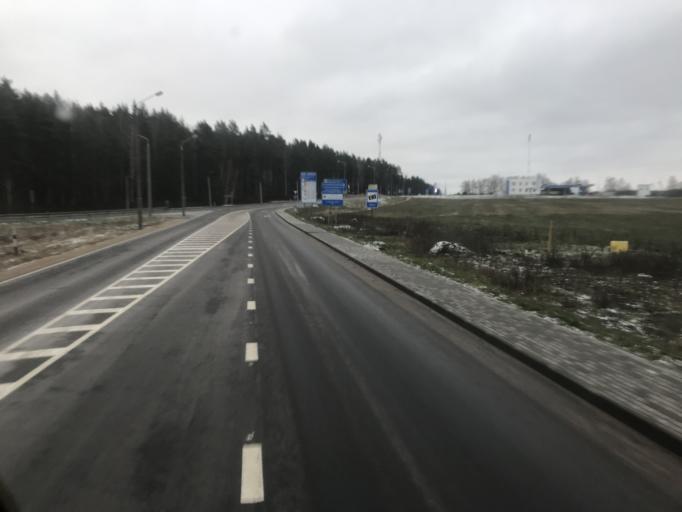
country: BY
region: Grodnenskaya
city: Vyalikaya Byerastavitsa
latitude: 53.1215
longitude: 23.9060
